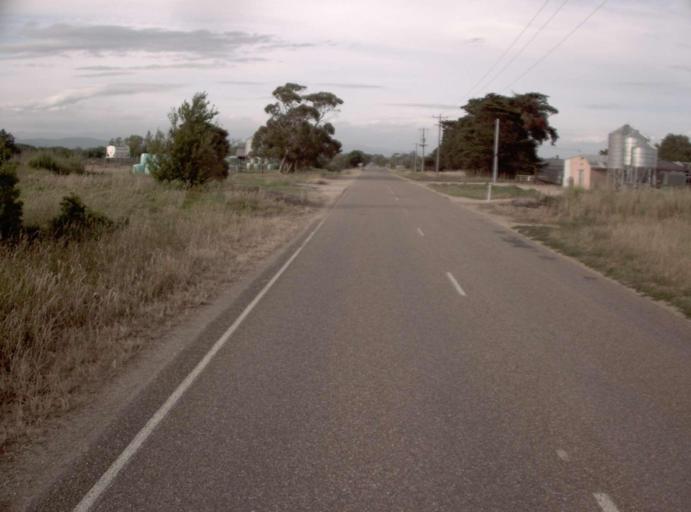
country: AU
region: Victoria
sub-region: Wellington
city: Heyfield
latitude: -37.9857
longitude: 146.8872
